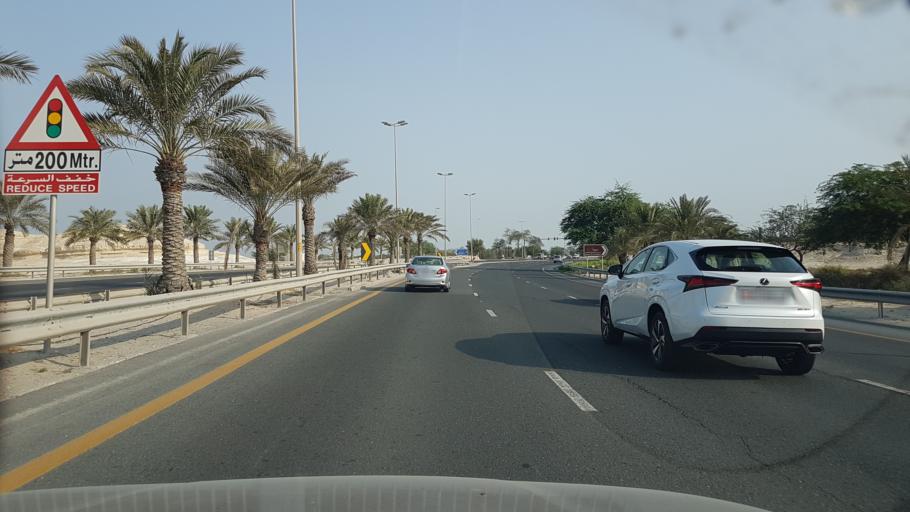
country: BH
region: Central Governorate
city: Dar Kulayb
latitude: 26.0687
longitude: 50.5237
